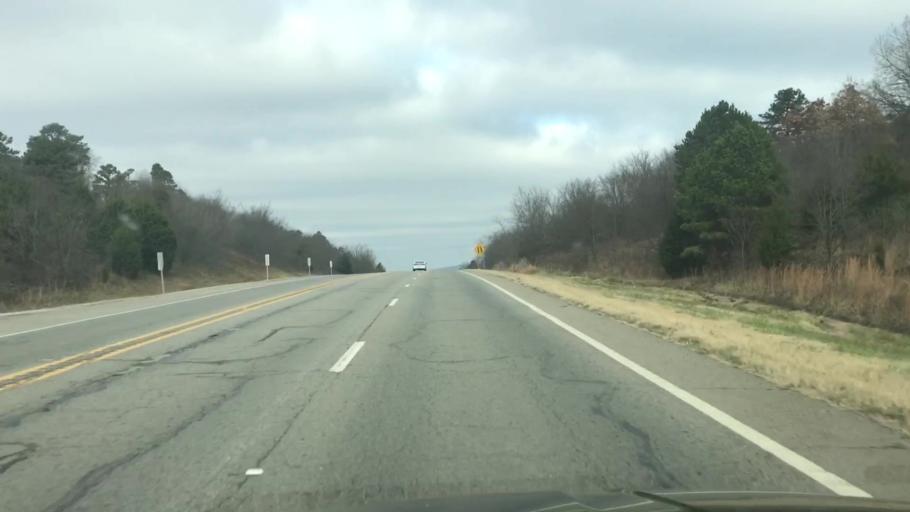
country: US
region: Arkansas
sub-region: Scott County
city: Waldron
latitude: 34.8613
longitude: -94.0713
